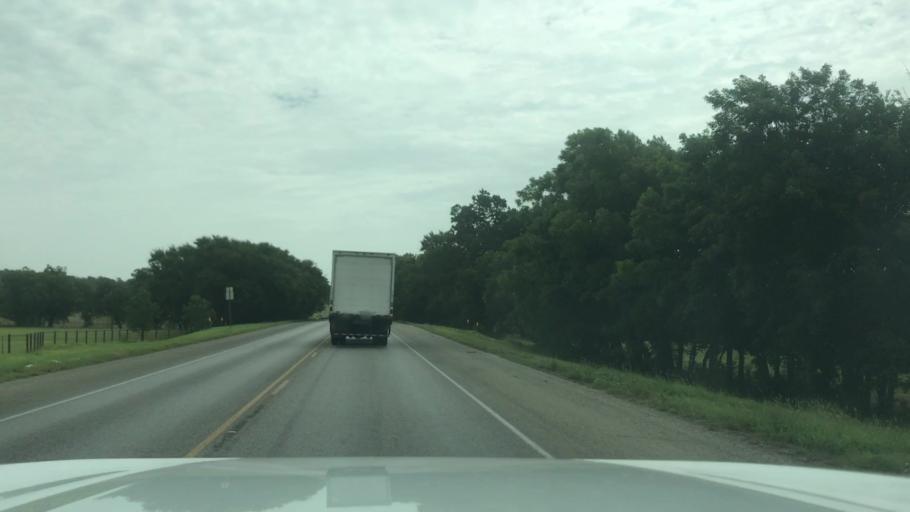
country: US
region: Texas
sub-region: Comanche County
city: De Leon
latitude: 32.0937
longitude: -98.4506
